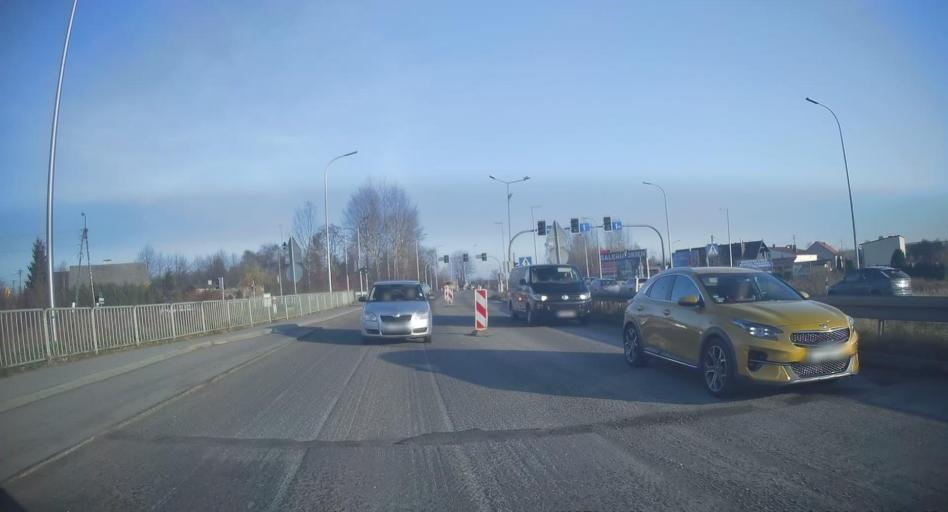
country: PL
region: Lesser Poland Voivodeship
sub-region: Powiat olkuski
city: Boleslaw
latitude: 50.3082
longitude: 19.4691
